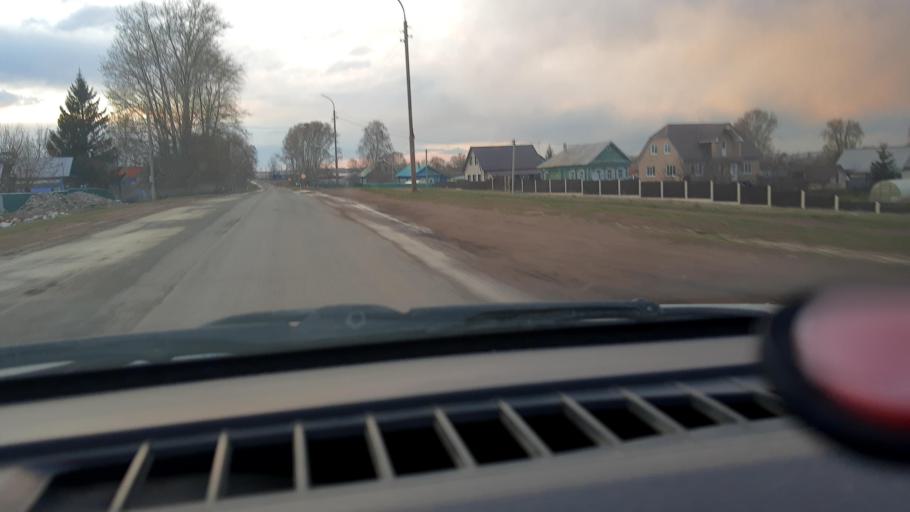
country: RU
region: Bashkortostan
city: Asanovo
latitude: 54.9569
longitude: 55.5535
